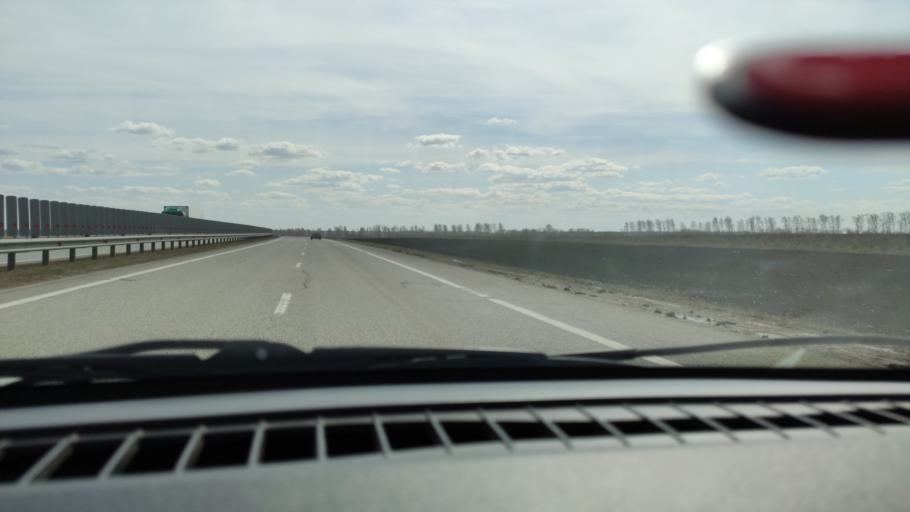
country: RU
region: Bashkortostan
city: Kushnarenkovo
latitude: 55.0865
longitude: 55.2566
